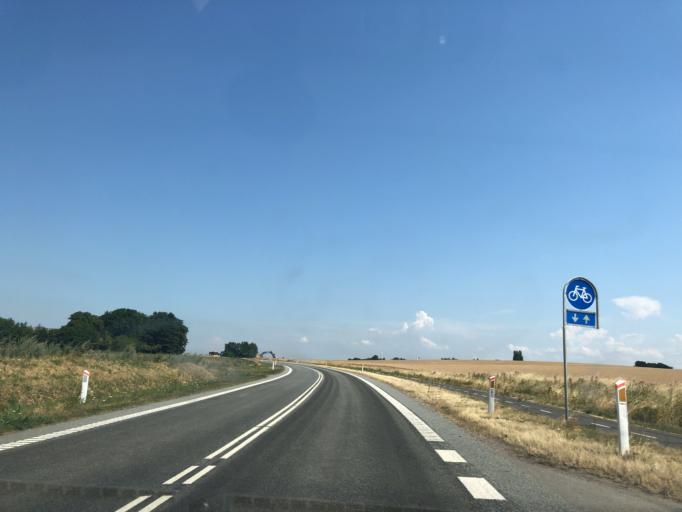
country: DK
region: Zealand
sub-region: Slagelse Kommune
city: Skaelskor
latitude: 55.2185
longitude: 11.3010
